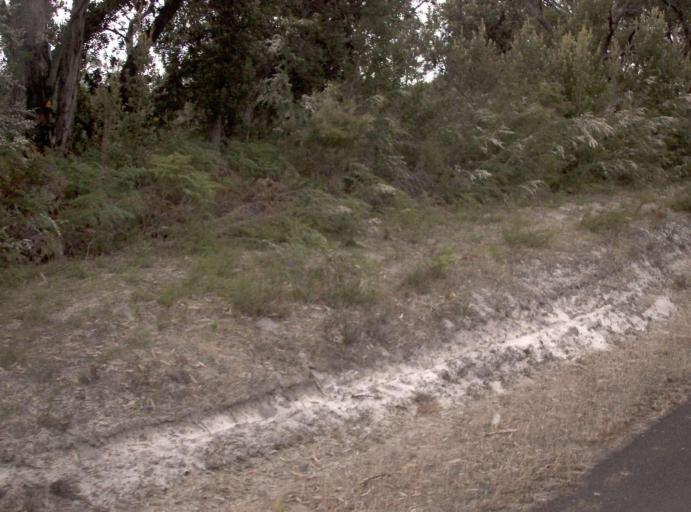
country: AU
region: Victoria
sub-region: Wellington
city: Sale
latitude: -38.3397
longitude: 147.0072
